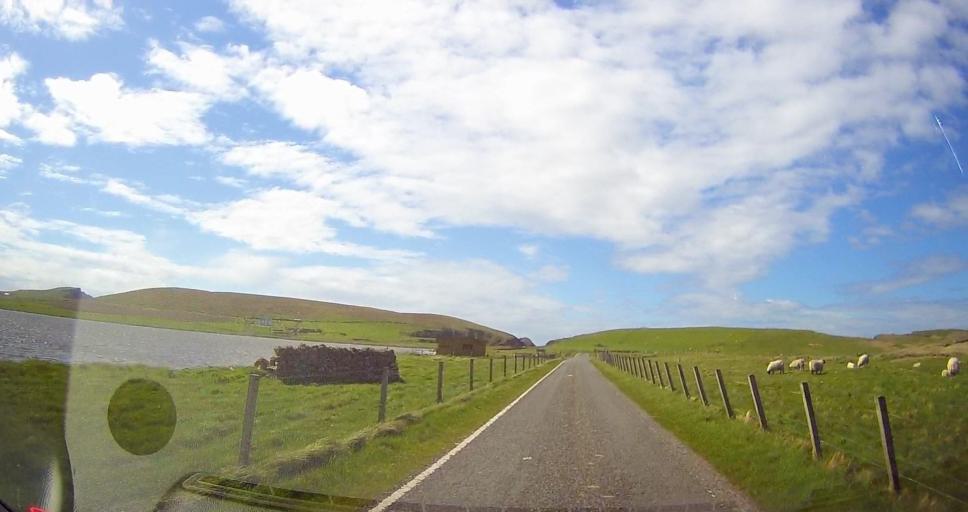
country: GB
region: Scotland
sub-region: Shetland Islands
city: Sandwick
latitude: 59.9425
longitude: -1.3372
